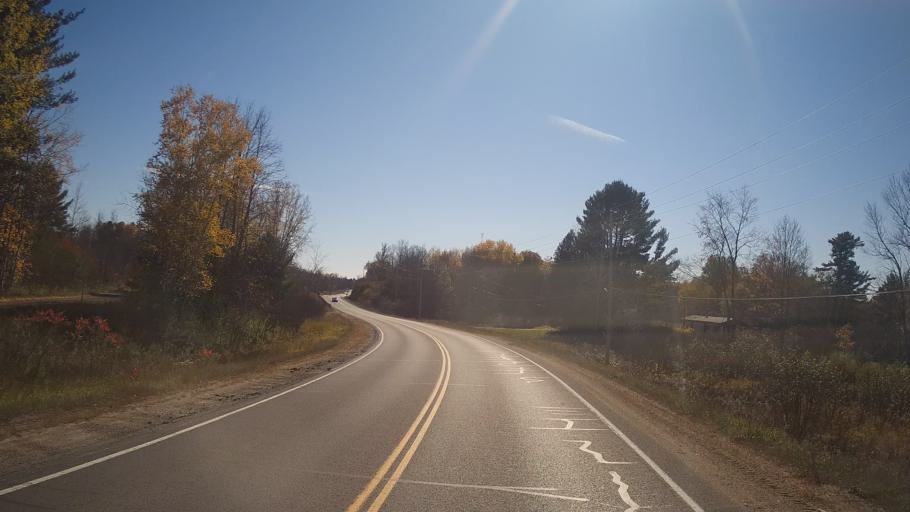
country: CA
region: Ontario
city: Kingston
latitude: 44.5491
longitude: -76.6781
